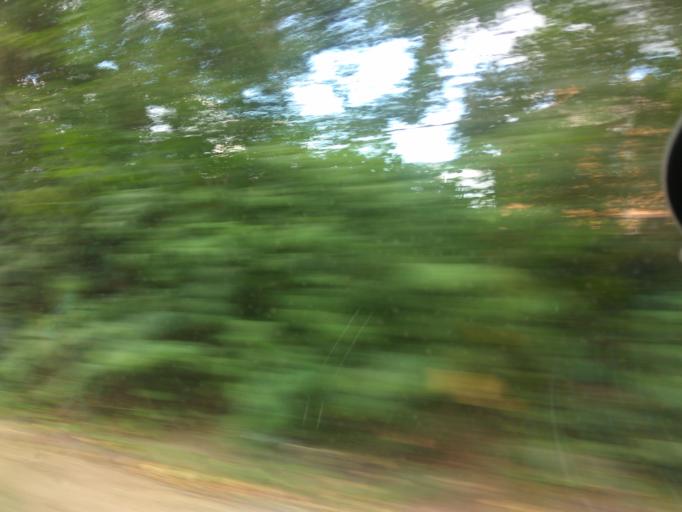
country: RU
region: Moskovskaya
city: Bronnitsy
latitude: 55.4618
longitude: 38.2742
